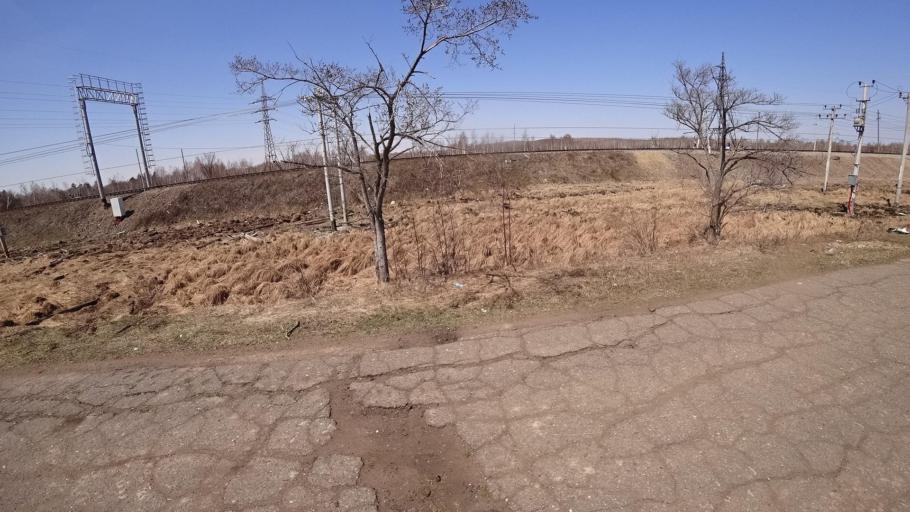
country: RU
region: Khabarovsk Krai
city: Khurba
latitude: 50.4021
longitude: 136.8673
